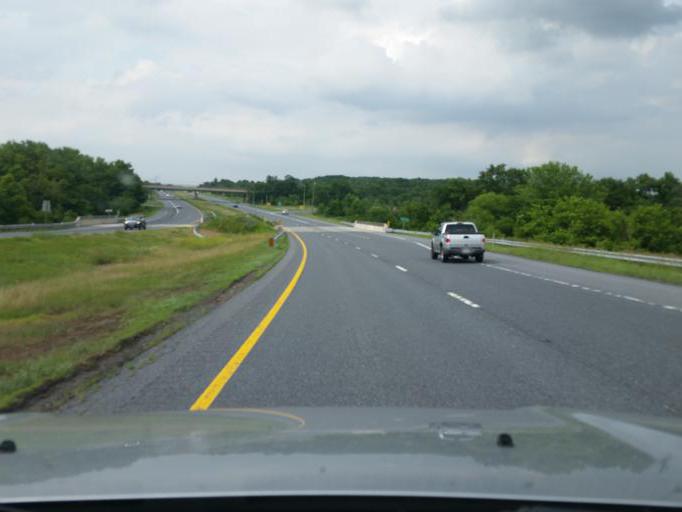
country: US
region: Maryland
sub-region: Frederick County
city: Emmitsburg
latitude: 39.6989
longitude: -77.3156
